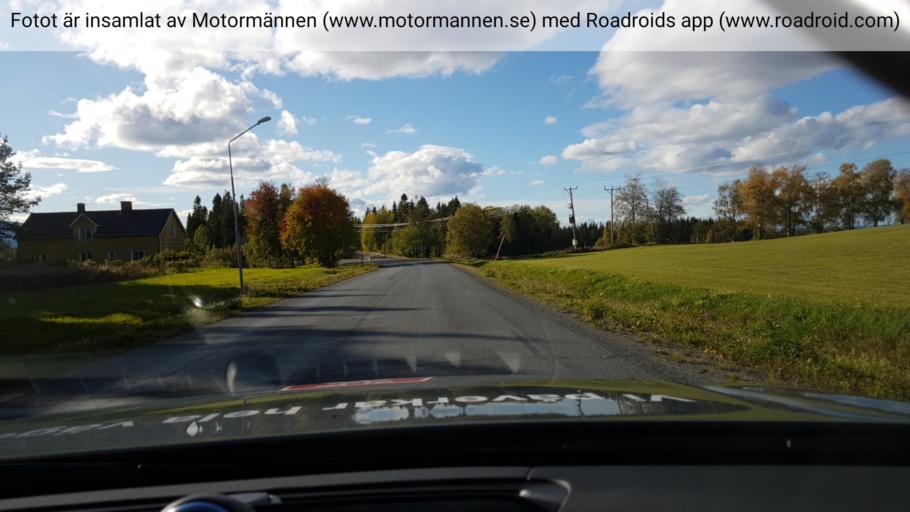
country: SE
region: Jaemtland
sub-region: Krokoms Kommun
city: Valla
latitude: 63.1854
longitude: 14.0261
